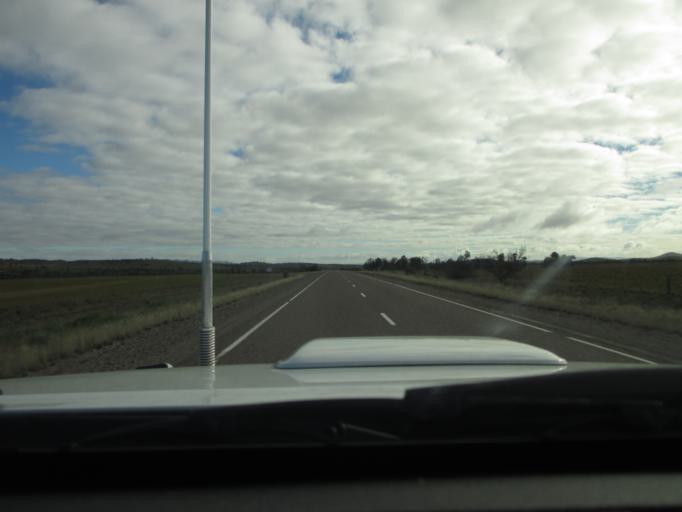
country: AU
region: South Australia
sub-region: Peterborough
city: Peterborough
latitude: -32.5365
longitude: 138.5569
